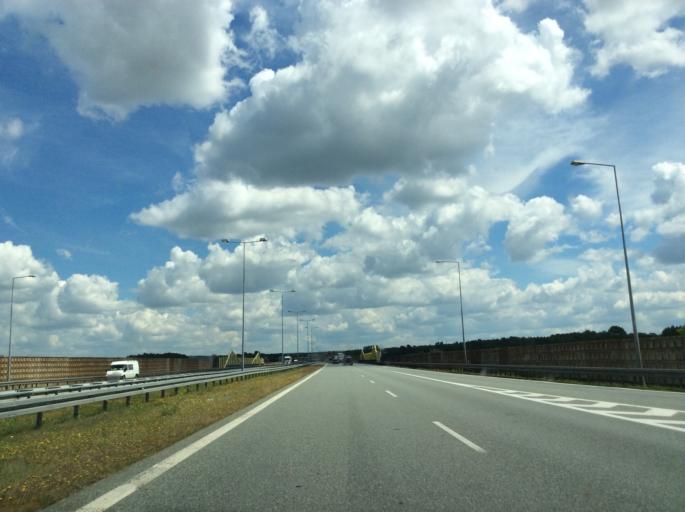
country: PL
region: Greater Poland Voivodeship
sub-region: Powiat koninski
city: Stare Miasto
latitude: 52.1622
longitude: 18.2135
